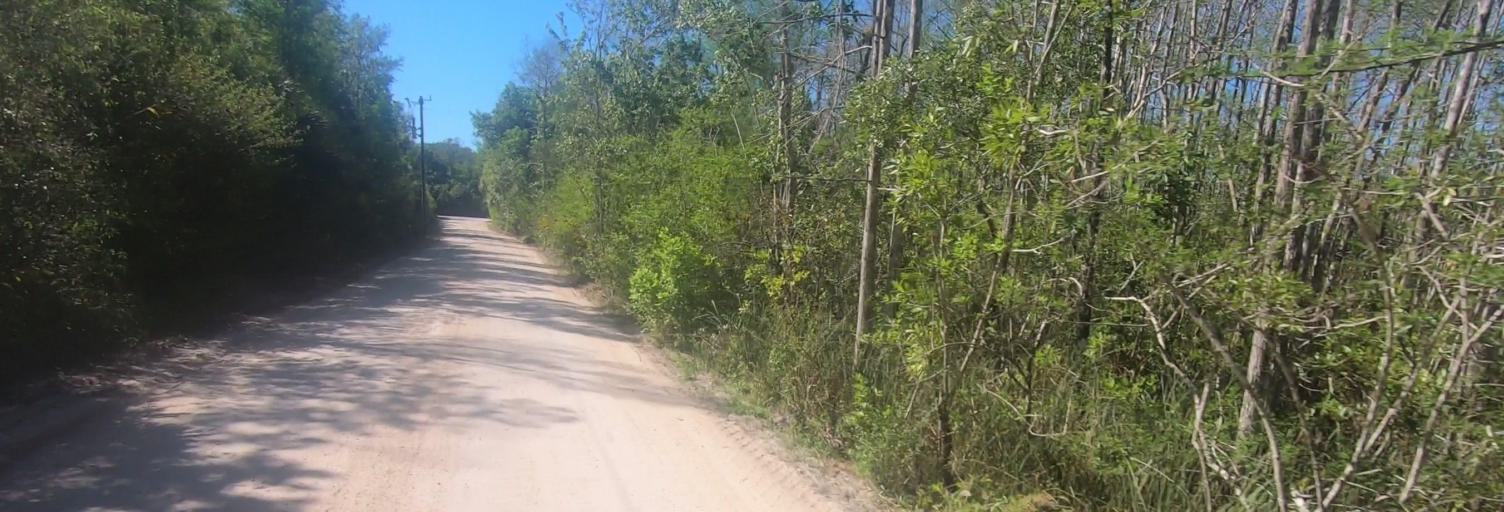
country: US
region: Florida
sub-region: Collier County
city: Marco
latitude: 25.8786
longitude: -81.2300
